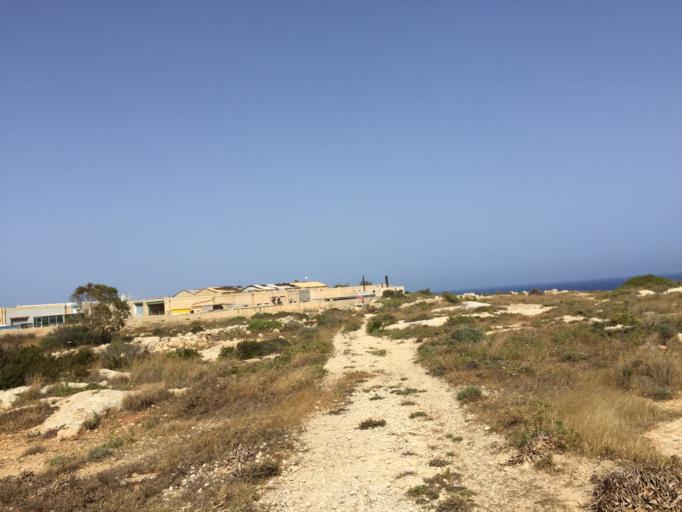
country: MT
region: Birzebbuga
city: Birzebbuga
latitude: 35.8073
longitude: 14.5128
